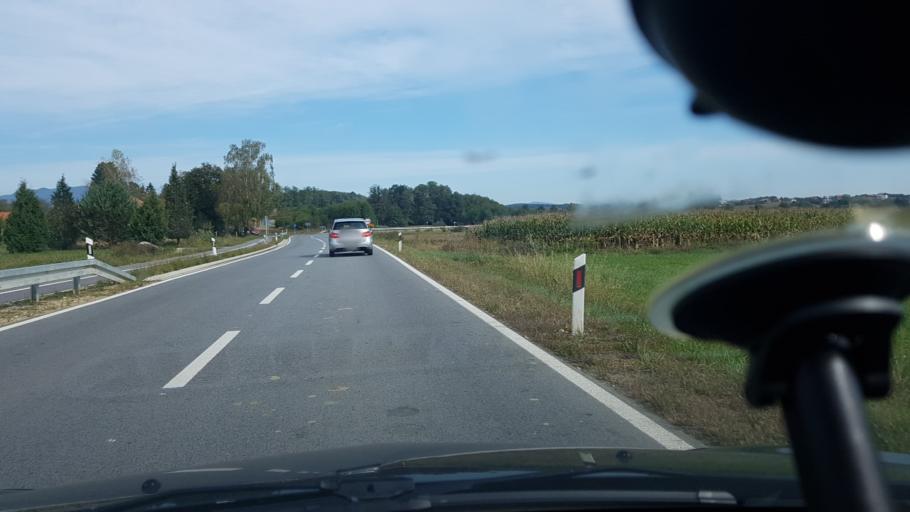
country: HR
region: Krapinsko-Zagorska
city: Marija Bistrica
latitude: 46.0550
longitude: 16.1517
